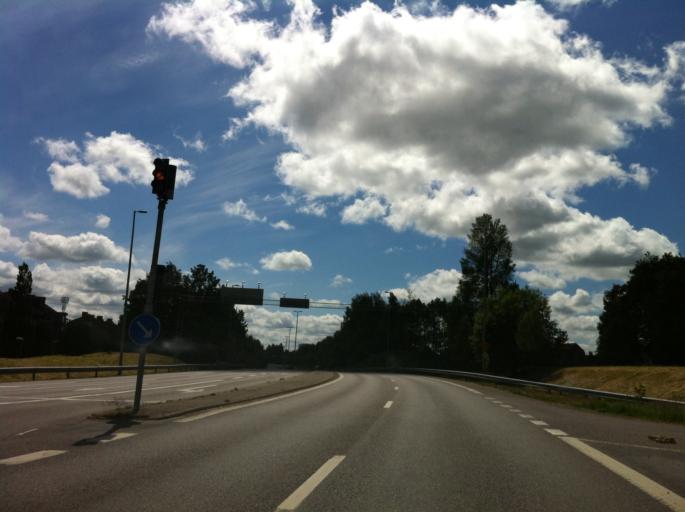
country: SE
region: Vaestra Goetaland
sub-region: Trollhattan
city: Trollhattan
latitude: 58.2961
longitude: 12.3240
